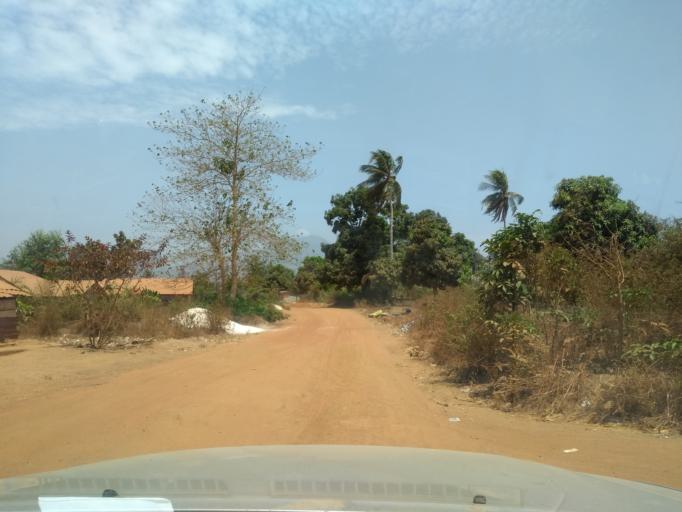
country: GN
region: Kindia
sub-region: Prefecture de Dubreka
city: Dubreka
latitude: 9.7865
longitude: -13.5408
